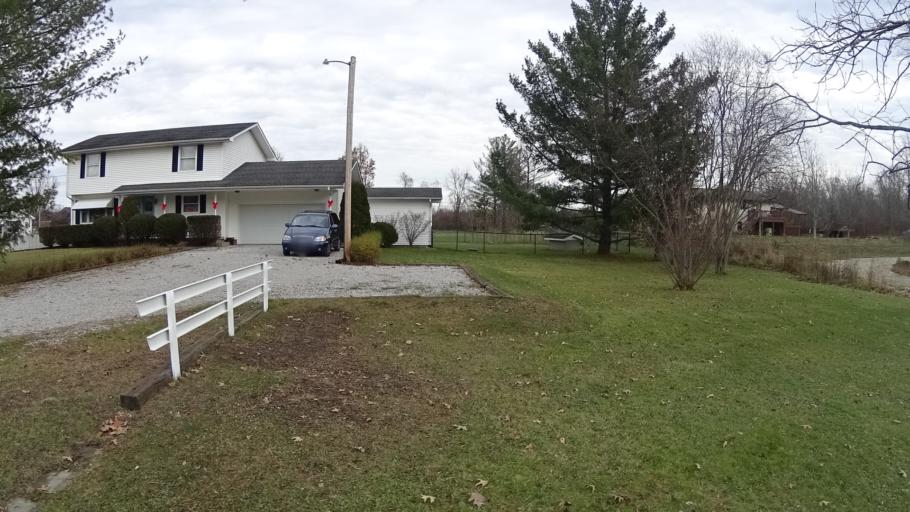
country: US
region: Ohio
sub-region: Cuyahoga County
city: Olmsted Falls
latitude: 41.3105
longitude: -81.9074
